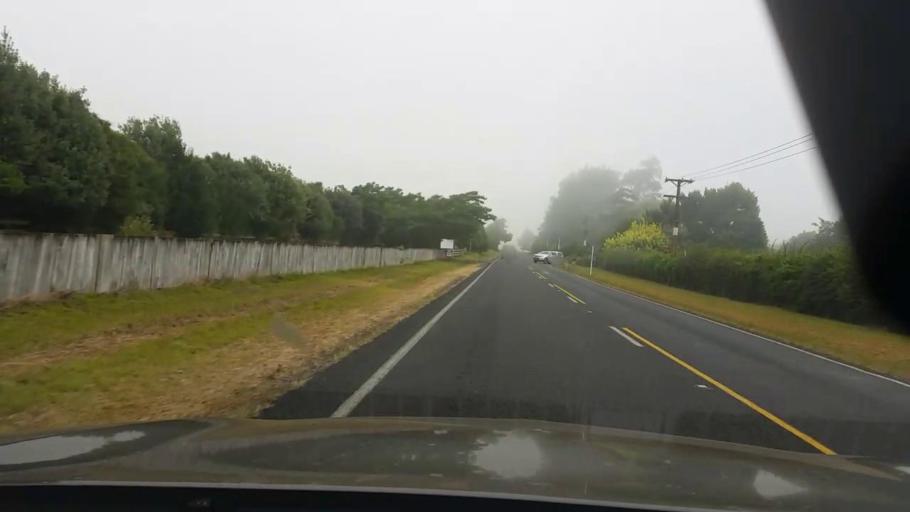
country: NZ
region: Waikato
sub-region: Hamilton City
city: Hamilton
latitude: -37.6504
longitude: 175.2980
